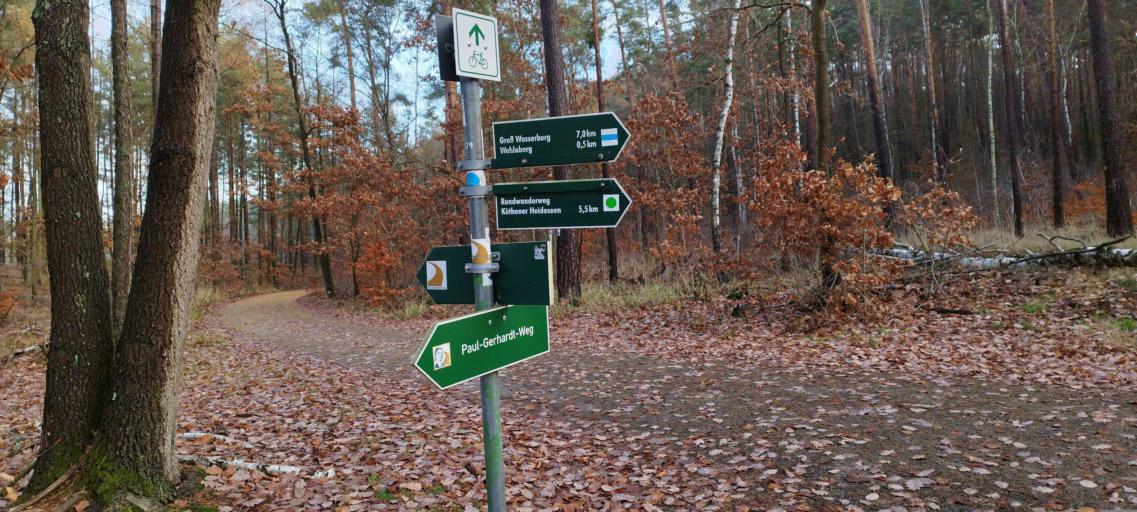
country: DE
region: Brandenburg
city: Munchehofe
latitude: 52.0644
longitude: 13.7984
